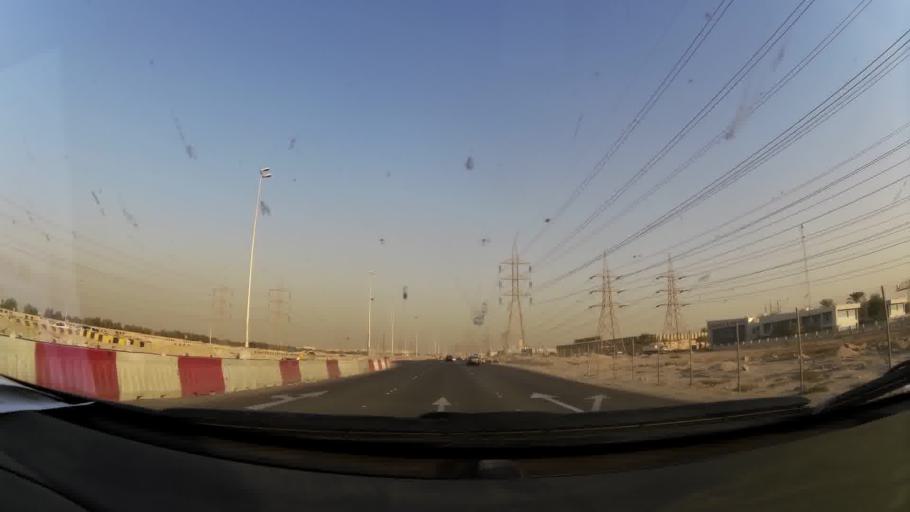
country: KW
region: Al Asimah
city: Ar Rabiyah
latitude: 29.2949
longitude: 47.8404
